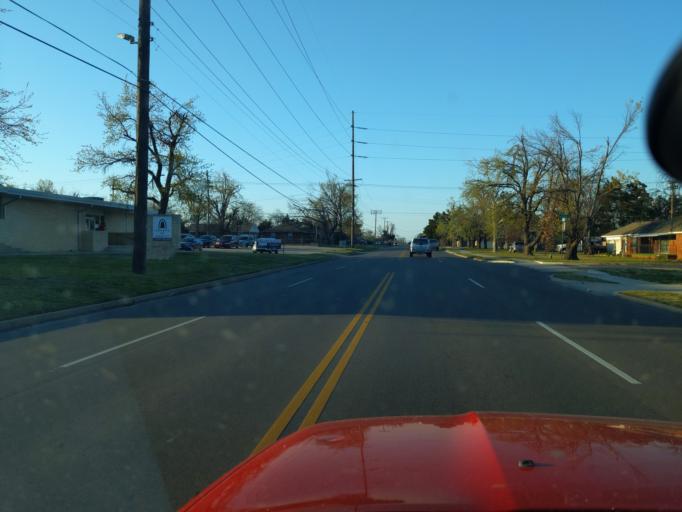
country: US
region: Oklahoma
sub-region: Oklahoma County
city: Oklahoma City
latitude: 35.4127
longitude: -97.5214
